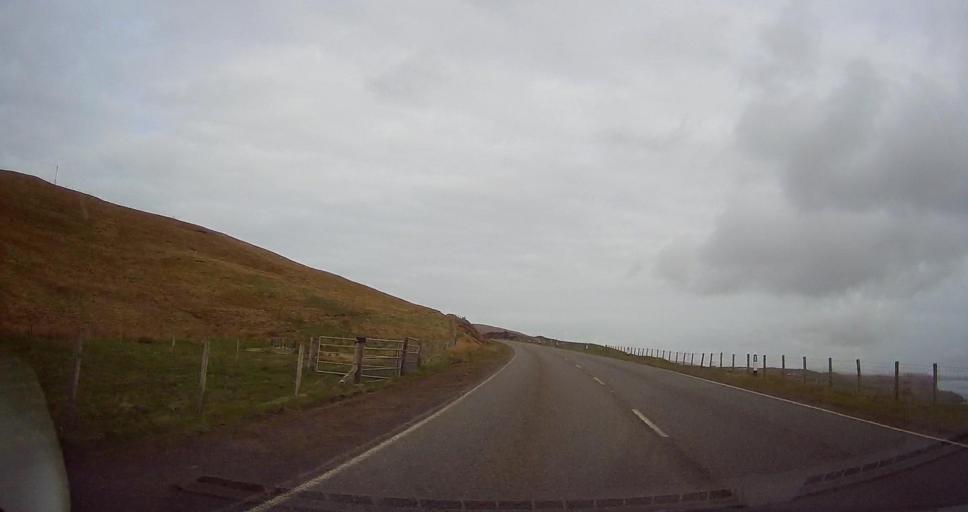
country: GB
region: Scotland
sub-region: Shetland Islands
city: Sandwick
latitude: 60.0636
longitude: -1.2216
